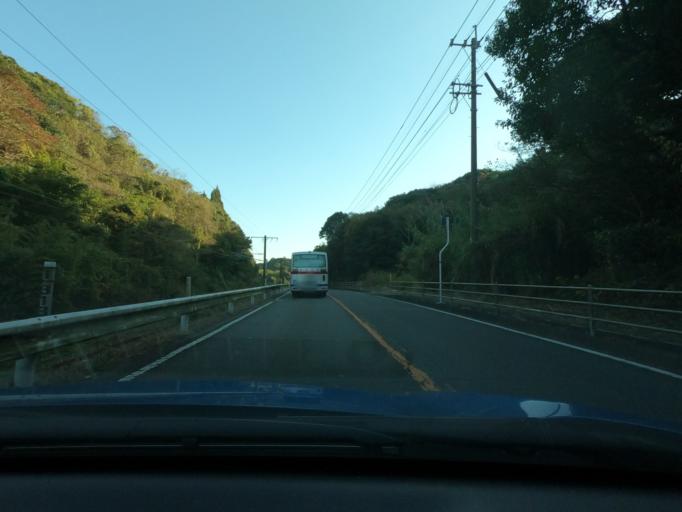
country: JP
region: Kagoshima
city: Akune
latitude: 31.9972
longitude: 130.1965
